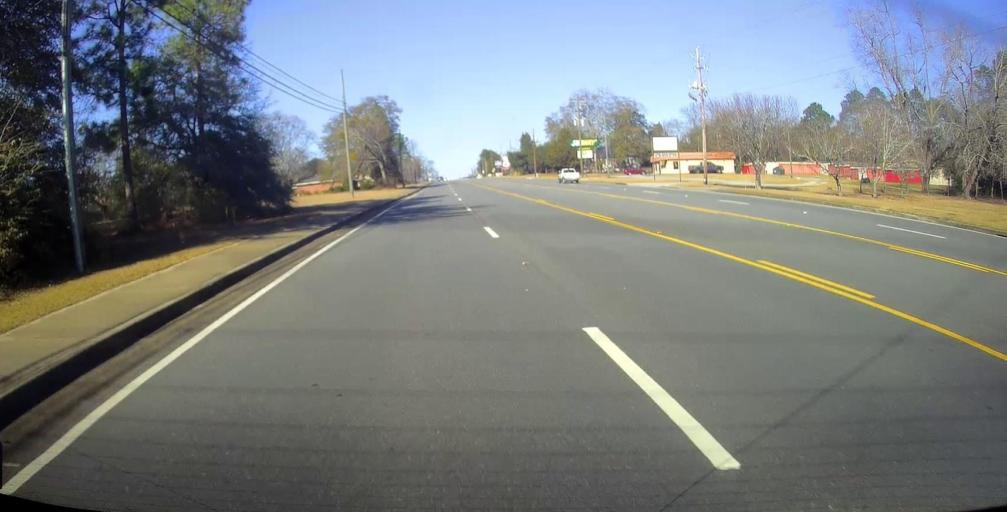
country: US
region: Georgia
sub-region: Taylor County
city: Butler
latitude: 32.5513
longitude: -84.2404
